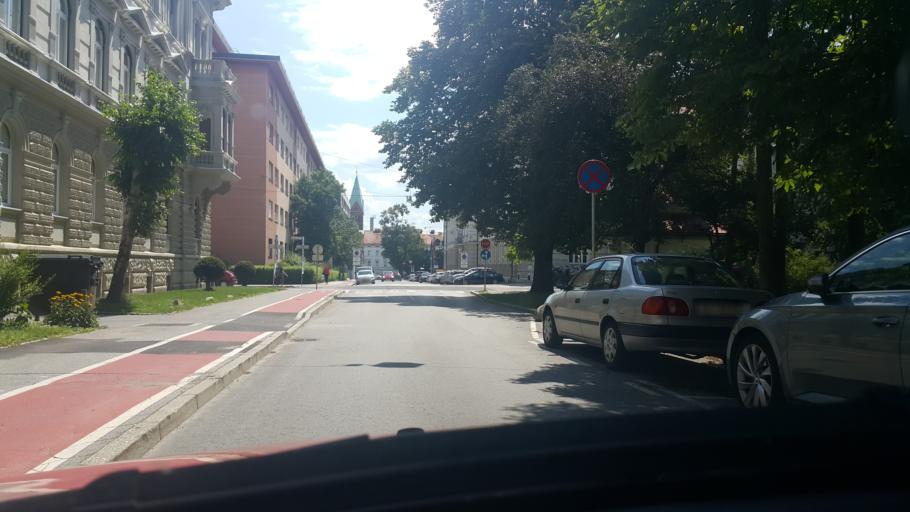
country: SI
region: Maribor
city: Maribor
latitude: 46.5635
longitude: 15.6500
